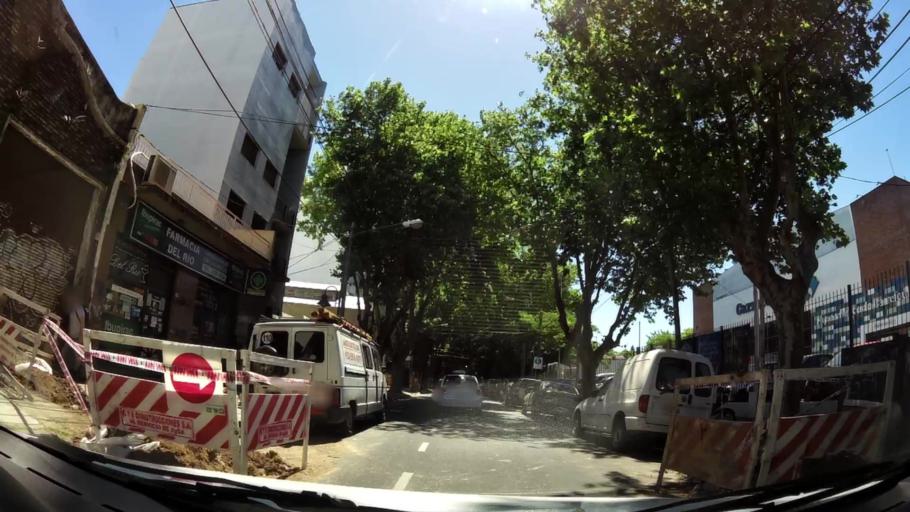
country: AR
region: Buenos Aires
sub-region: Partido de Vicente Lopez
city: Olivos
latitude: -34.5159
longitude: -58.4953
